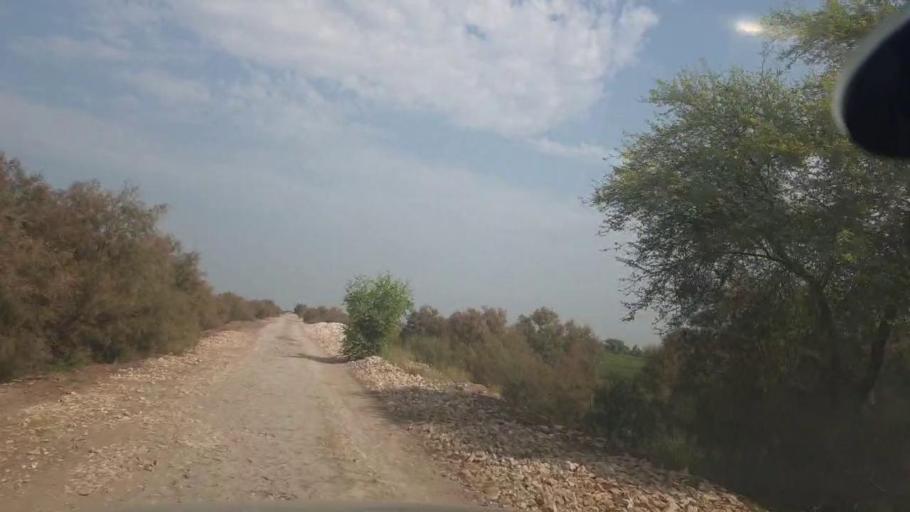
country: PK
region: Balochistan
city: Mehrabpur
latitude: 28.0951
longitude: 68.0938
